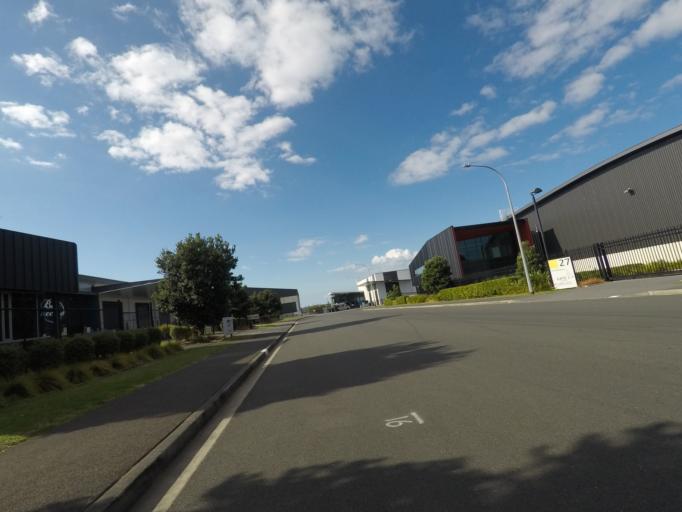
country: NZ
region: Auckland
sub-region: Auckland
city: Rosebank
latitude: -36.8825
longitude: 174.6834
